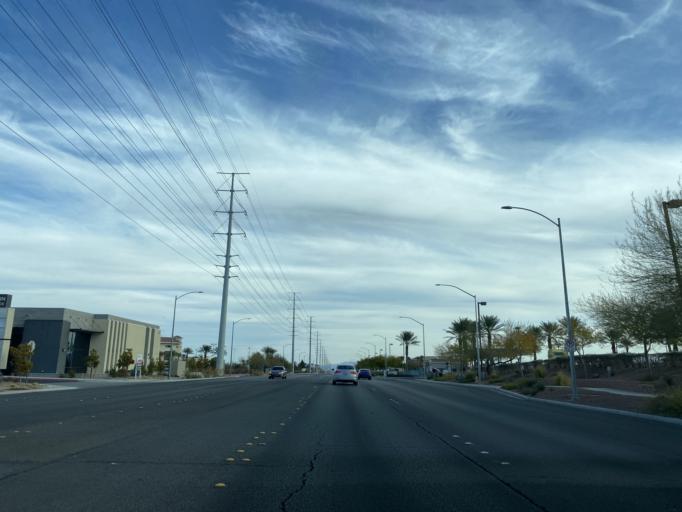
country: US
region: Nevada
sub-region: Clark County
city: Enterprise
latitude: 36.0555
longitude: -115.2760
